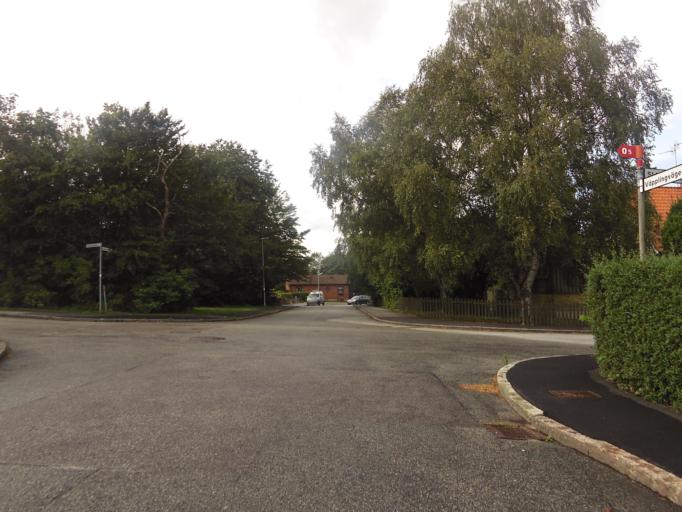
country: SE
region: Skane
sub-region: Lunds Kommun
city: Lund
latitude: 55.7178
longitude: 13.1758
